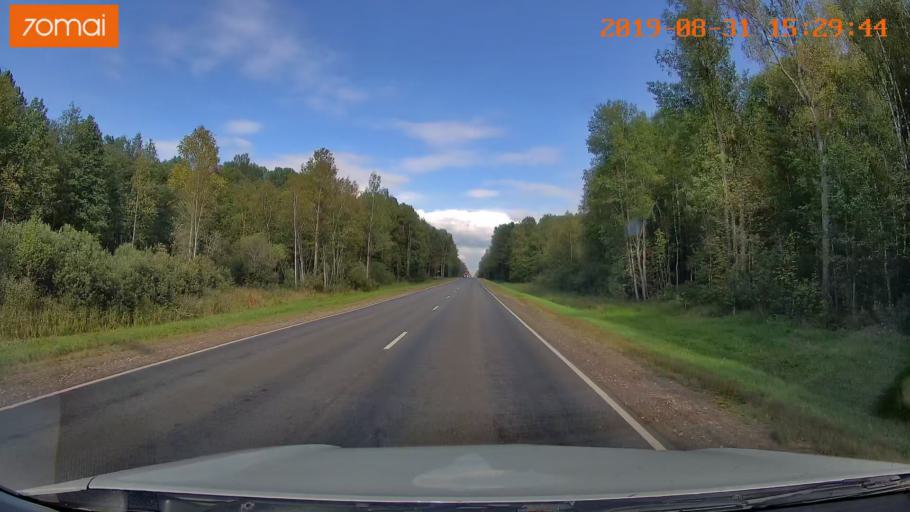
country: RU
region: Kaluga
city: Baryatino
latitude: 54.5709
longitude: 34.6130
